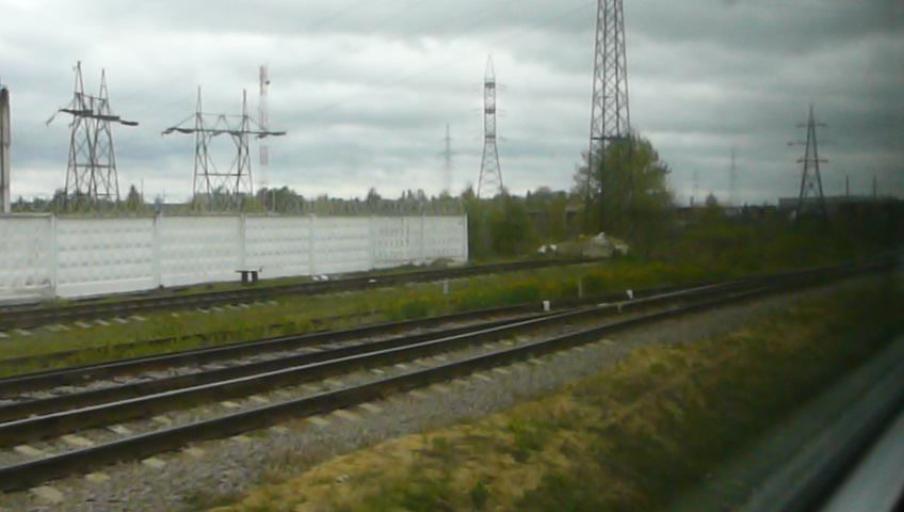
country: RU
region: Moskovskaya
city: Yegor'yevsk
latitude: 55.3961
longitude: 39.0041
